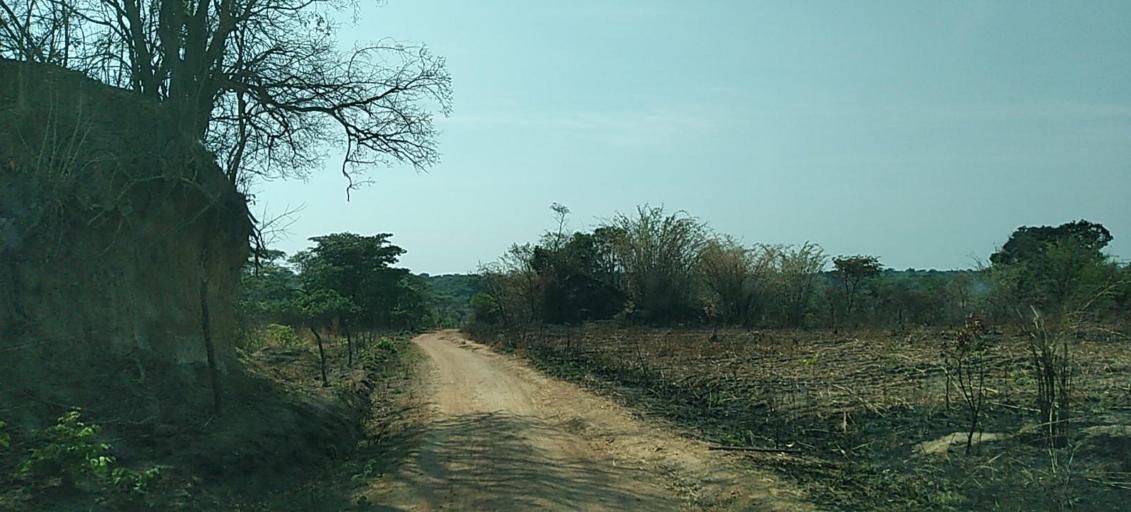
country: ZM
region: Copperbelt
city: Luanshya
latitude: -13.1903
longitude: 28.4765
